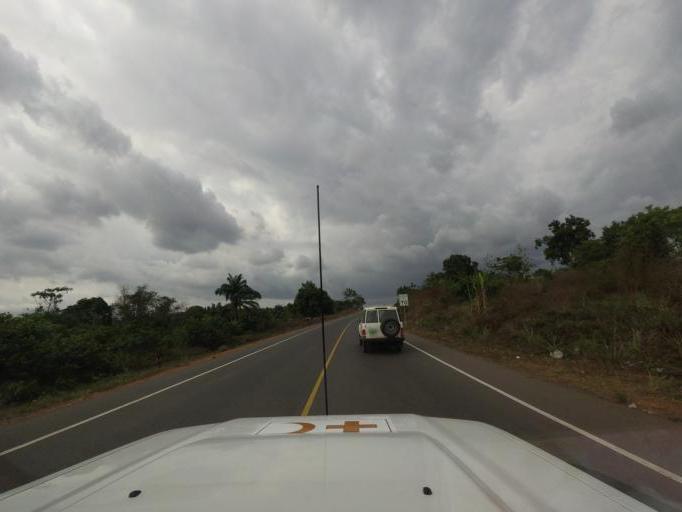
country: LR
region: Margibi
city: Kakata
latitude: 6.5690
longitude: -10.3200
